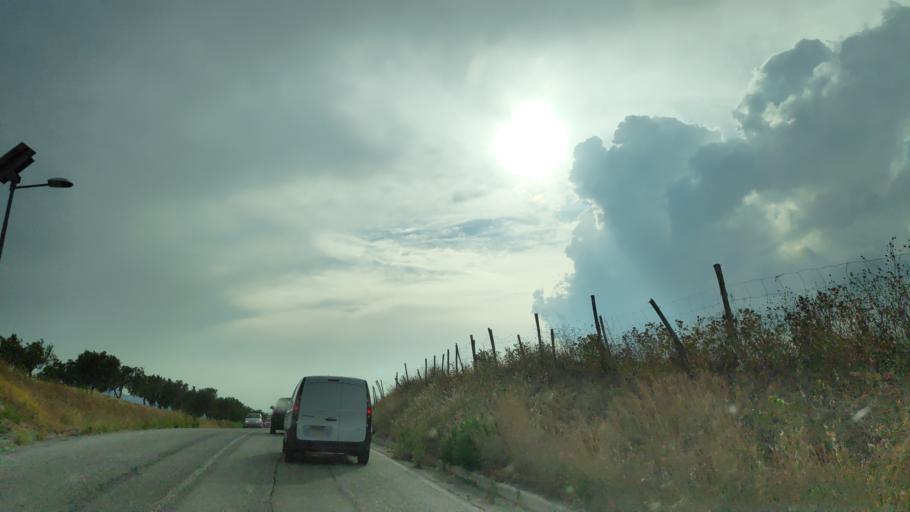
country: IT
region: Calabria
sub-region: Provincia di Catanzaro
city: Martelli-Laganosa
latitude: 38.6783
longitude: 16.5110
